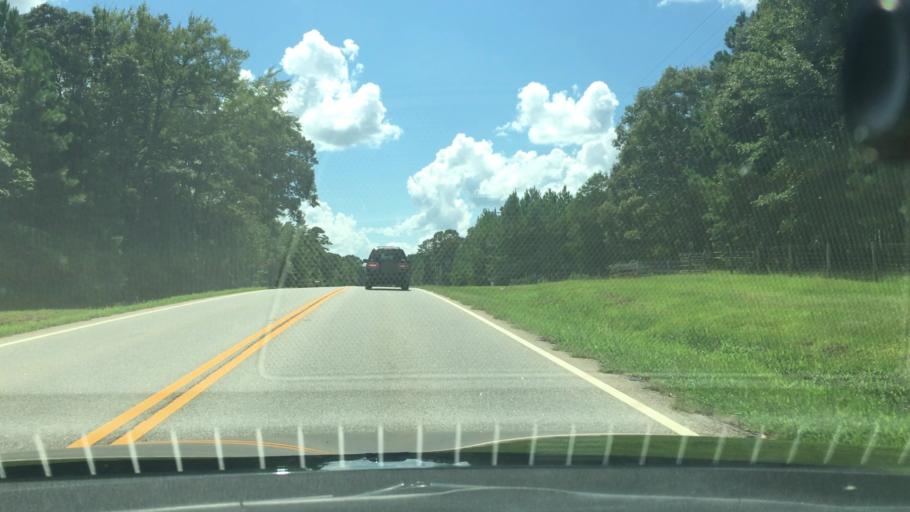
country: US
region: Georgia
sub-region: Putnam County
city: Eatonton
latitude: 33.3082
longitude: -83.4735
